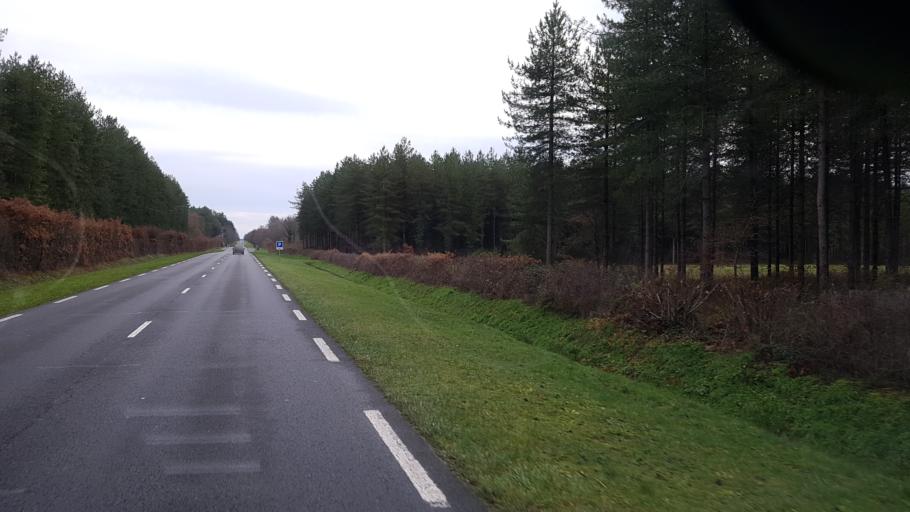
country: FR
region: Centre
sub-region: Departement du Loir-et-Cher
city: Lamotte-Beuvron
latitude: 47.6344
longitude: 2.0019
